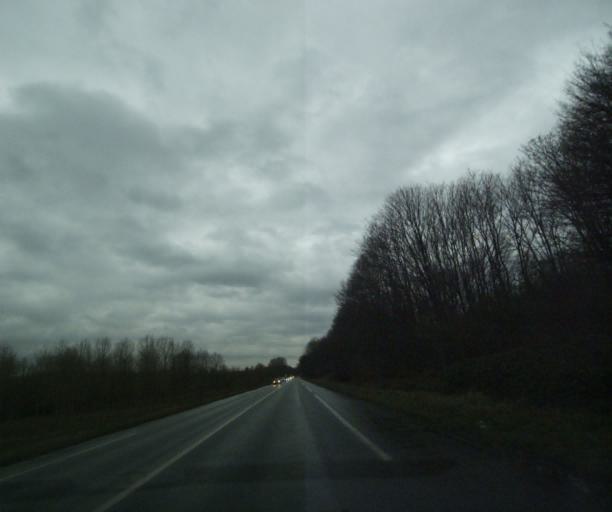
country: FR
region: Nord-Pas-de-Calais
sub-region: Departement du Nord
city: Vicq
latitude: 50.4135
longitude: 3.5891
